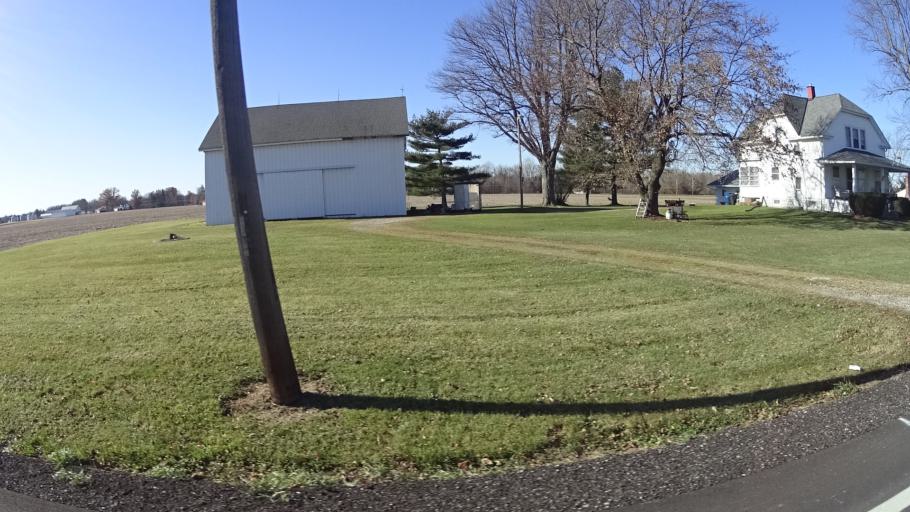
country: US
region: Ohio
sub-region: Lorain County
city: Elyria
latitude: 41.3110
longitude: -82.1177
